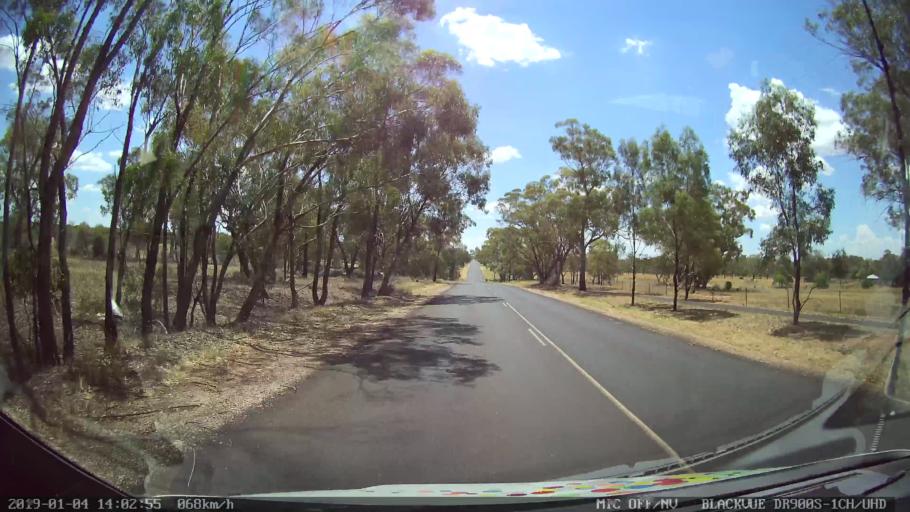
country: AU
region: New South Wales
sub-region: Dubbo Municipality
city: Dubbo
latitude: -32.2821
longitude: 148.5947
